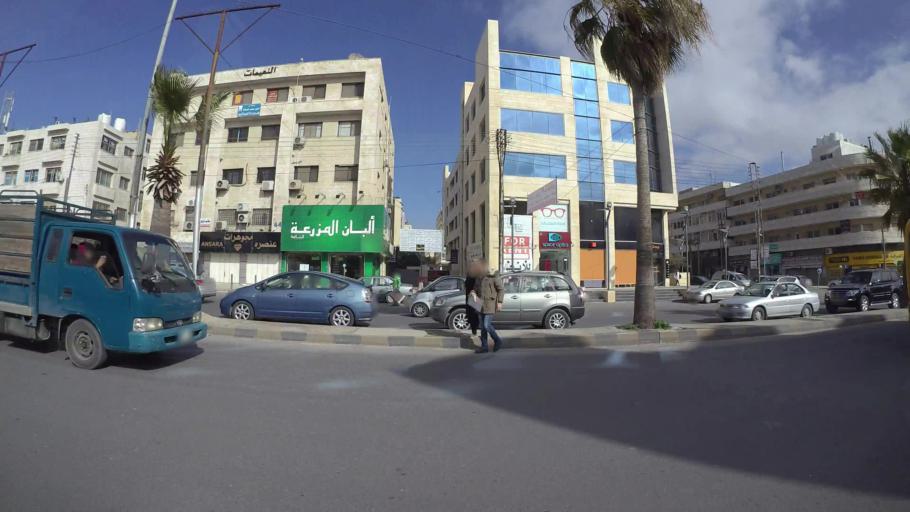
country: JO
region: Amman
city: Wadi as Sir
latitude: 31.9545
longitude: 35.8408
